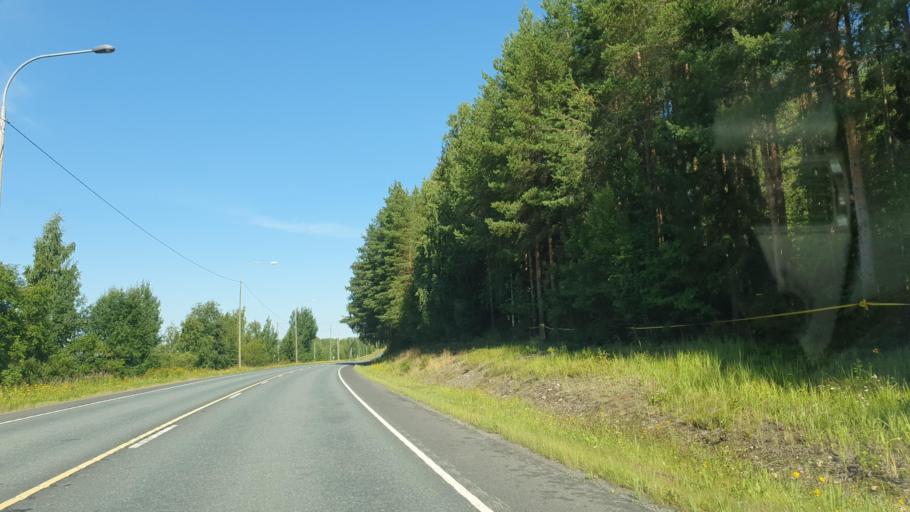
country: FI
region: Northern Savo
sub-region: Kuopio
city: Siilinjaervi
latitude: 63.1656
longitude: 27.5636
